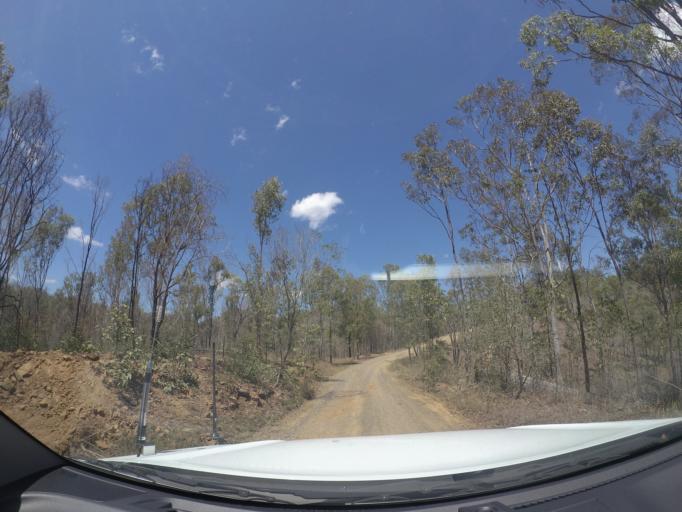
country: AU
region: Queensland
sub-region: Ipswich
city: Springfield Lakes
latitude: -27.8226
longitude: 152.8429
